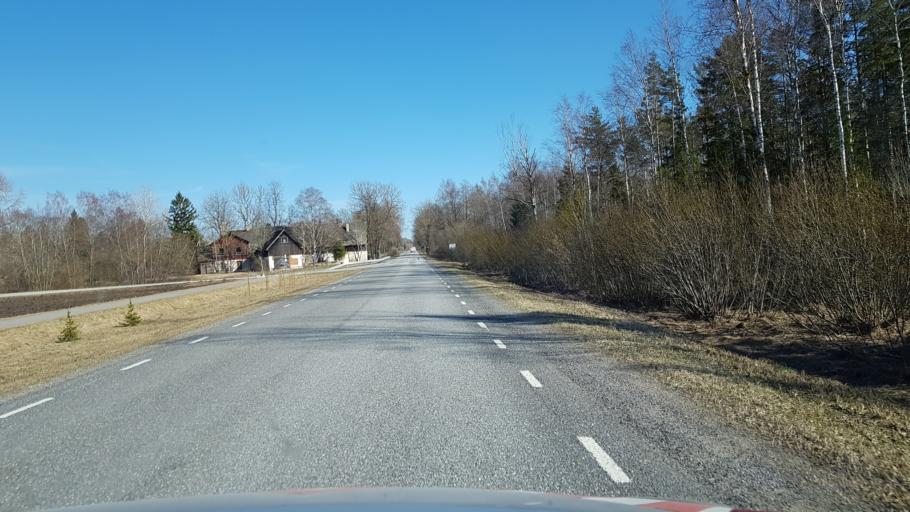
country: EE
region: Laeaene-Virumaa
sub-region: Rakke vald
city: Rakke
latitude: 58.9930
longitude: 26.2250
